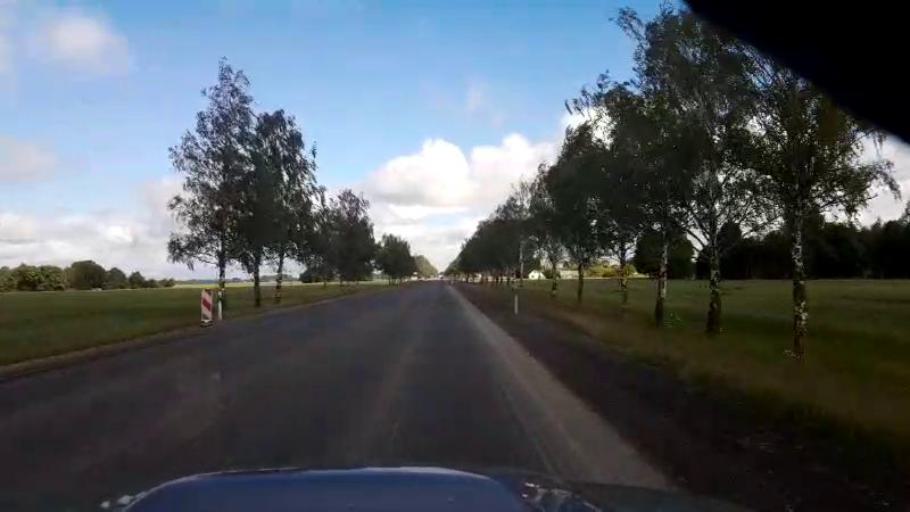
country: LV
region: Bauskas Rajons
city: Bauska
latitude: 56.3461
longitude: 24.2898
